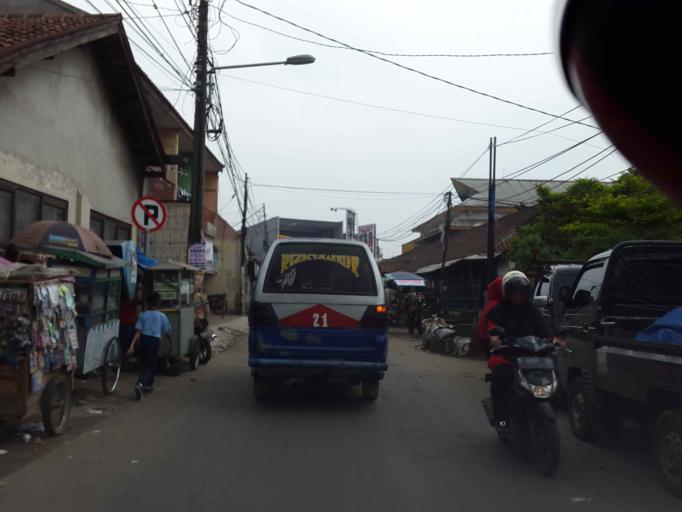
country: ID
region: West Java
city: Cimahi
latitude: -6.8986
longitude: 107.5558
